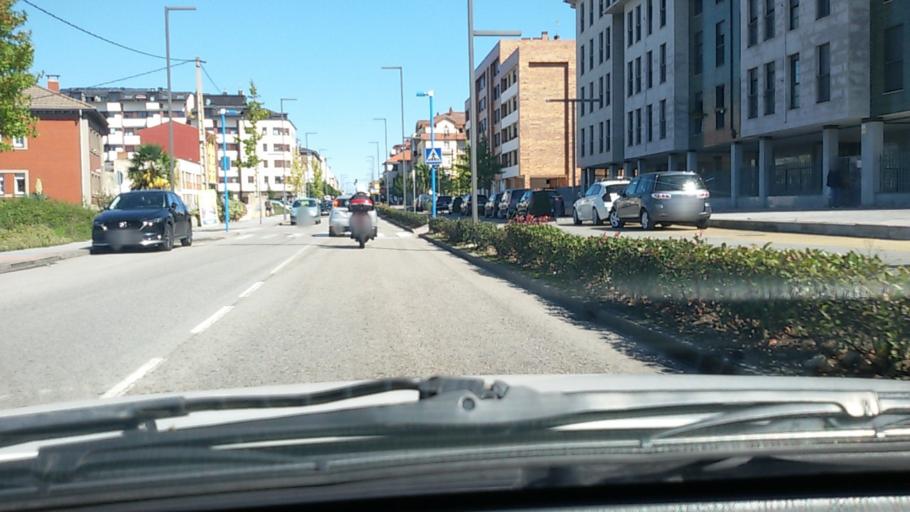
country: ES
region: Asturias
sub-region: Province of Asturias
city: Lugones
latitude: 43.3986
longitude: -5.8127
